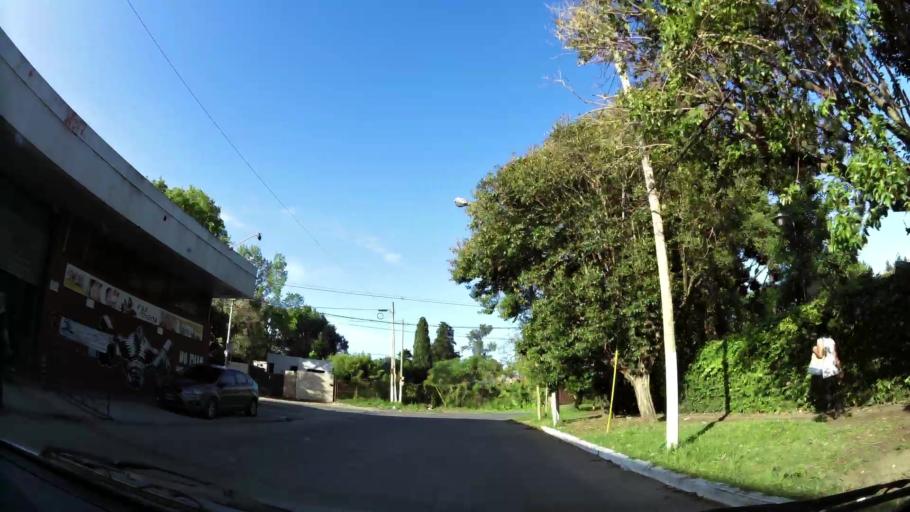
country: AR
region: Buenos Aires
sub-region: Partido de Quilmes
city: Quilmes
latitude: -34.7914
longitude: -58.2080
